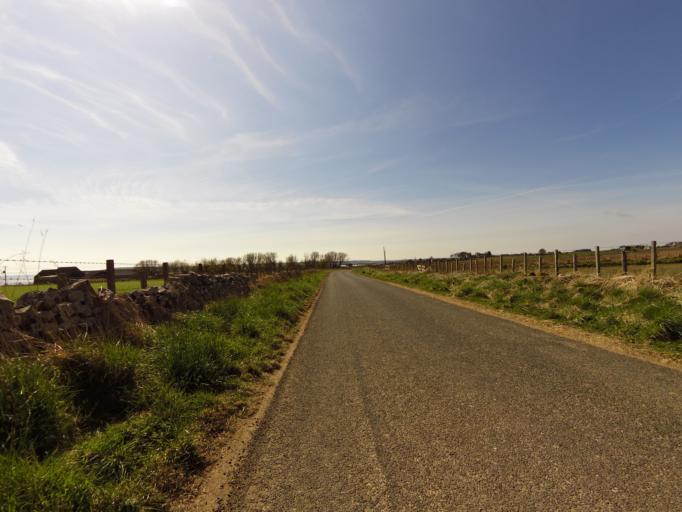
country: GB
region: Scotland
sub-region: Angus
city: Montrose
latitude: 56.6695
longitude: -2.5004
